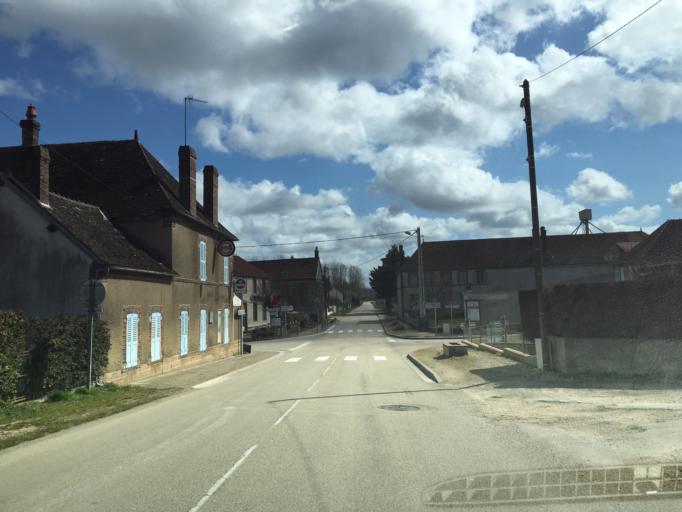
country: FR
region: Bourgogne
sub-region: Departement de l'Yonne
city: Aillant-sur-Tholon
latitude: 47.8438
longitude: 3.3934
